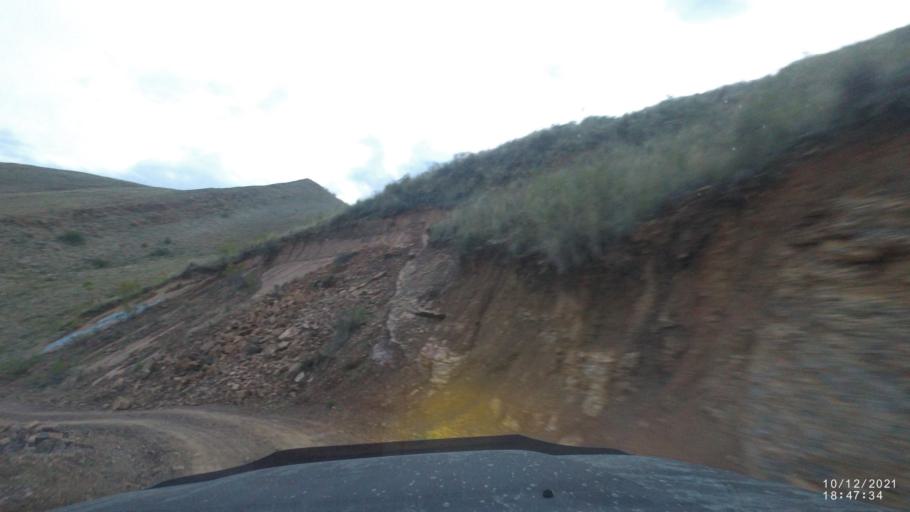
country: BO
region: Cochabamba
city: Tarata
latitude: -17.8802
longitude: -65.9748
